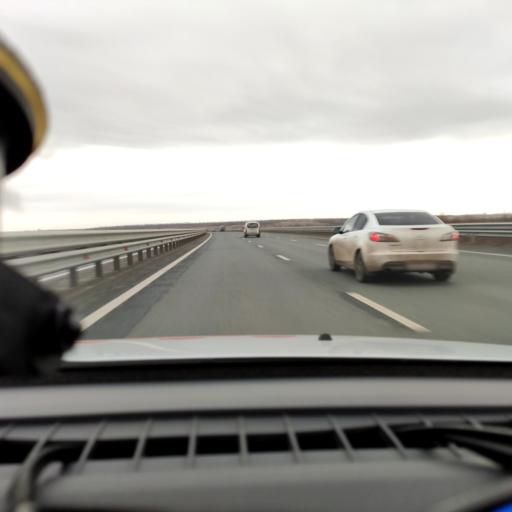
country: RU
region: Samara
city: Smyshlyayevka
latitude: 53.1658
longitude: 50.3197
